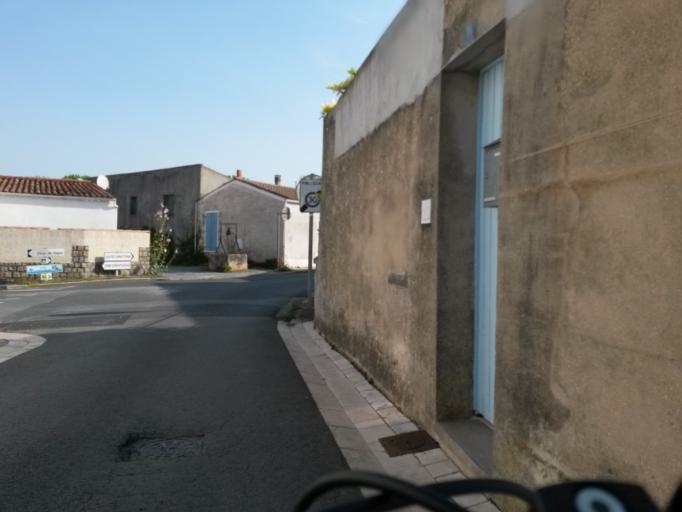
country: FR
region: Poitou-Charentes
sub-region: Departement de la Charente-Maritime
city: Marsilly
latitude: 46.2308
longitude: -1.1381
